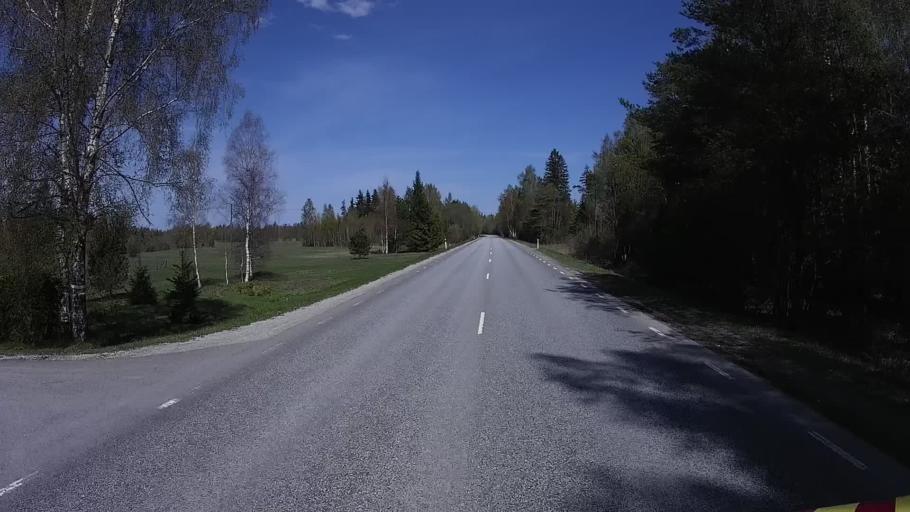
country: EE
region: Harju
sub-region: Keila linn
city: Keila
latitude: 59.2568
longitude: 24.2871
